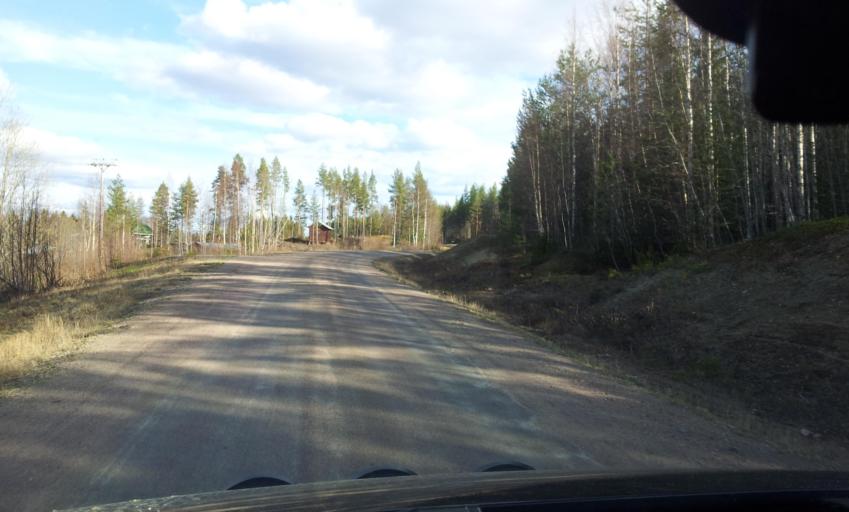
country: SE
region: Vaesternorrland
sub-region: Ange Kommun
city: Ange
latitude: 62.1769
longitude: 15.6340
